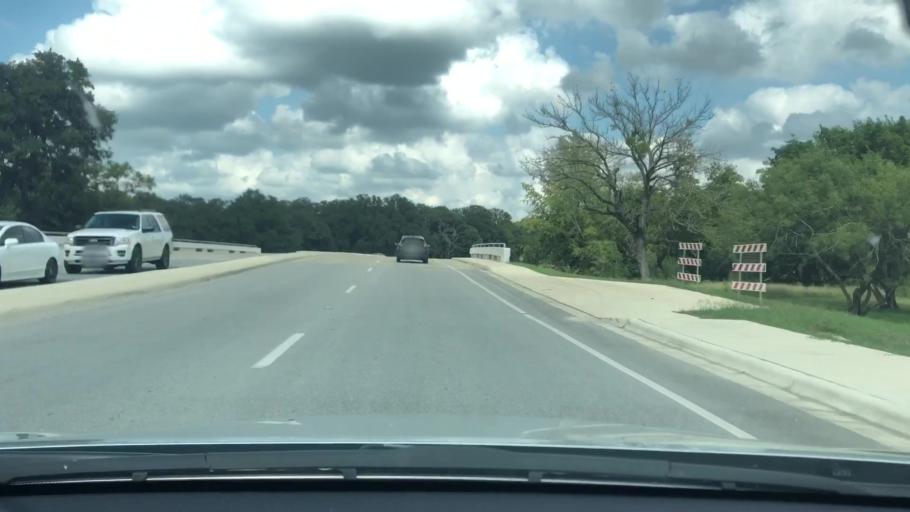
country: US
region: Texas
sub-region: Kendall County
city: Boerne
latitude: 29.7755
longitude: -98.7233
